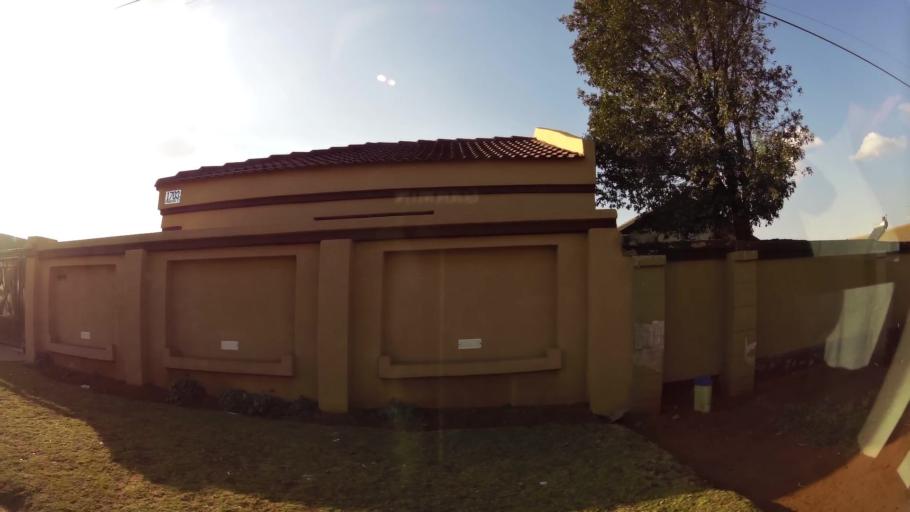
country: ZA
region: Gauteng
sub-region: Ekurhuleni Metropolitan Municipality
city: Tembisa
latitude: -25.9511
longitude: 28.2022
